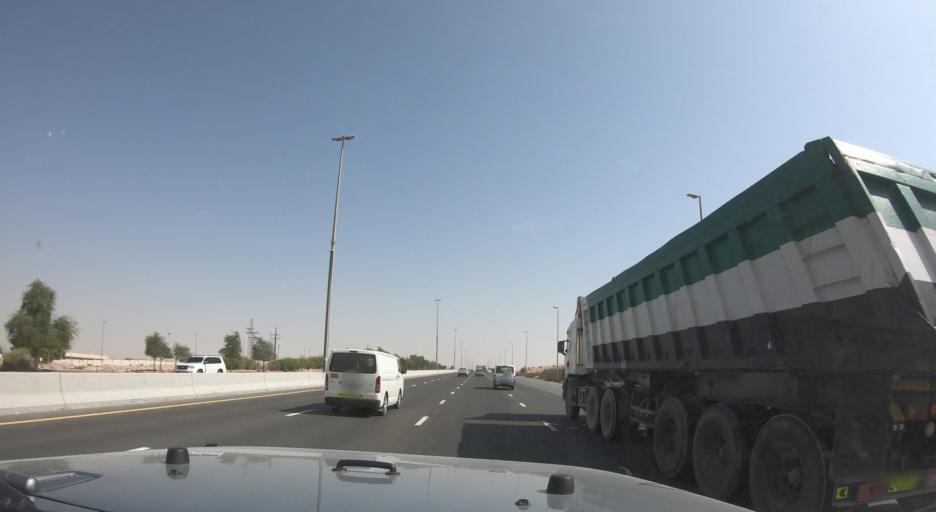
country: AE
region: Ash Shariqah
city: Sharjah
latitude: 25.1649
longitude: 55.4825
